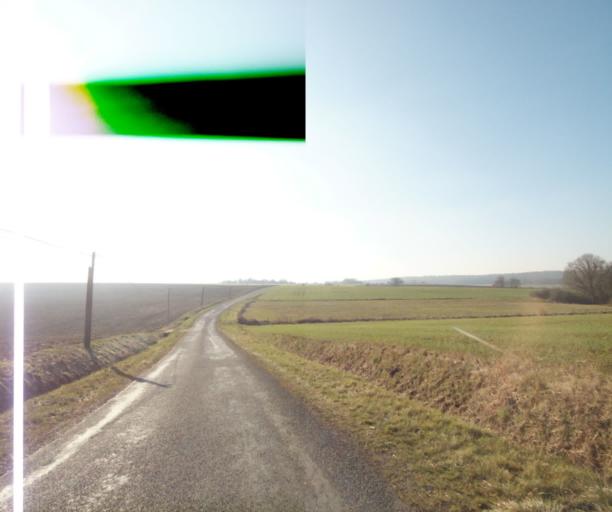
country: FR
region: Champagne-Ardenne
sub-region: Departement de la Haute-Marne
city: Bienville
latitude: 48.5317
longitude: 5.0072
